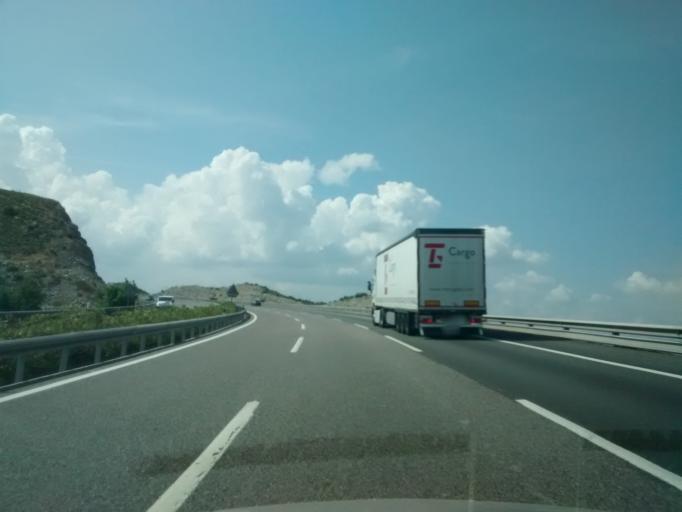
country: ES
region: Aragon
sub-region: Provincia de Zaragoza
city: Ricla
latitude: 41.4873
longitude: -1.4257
